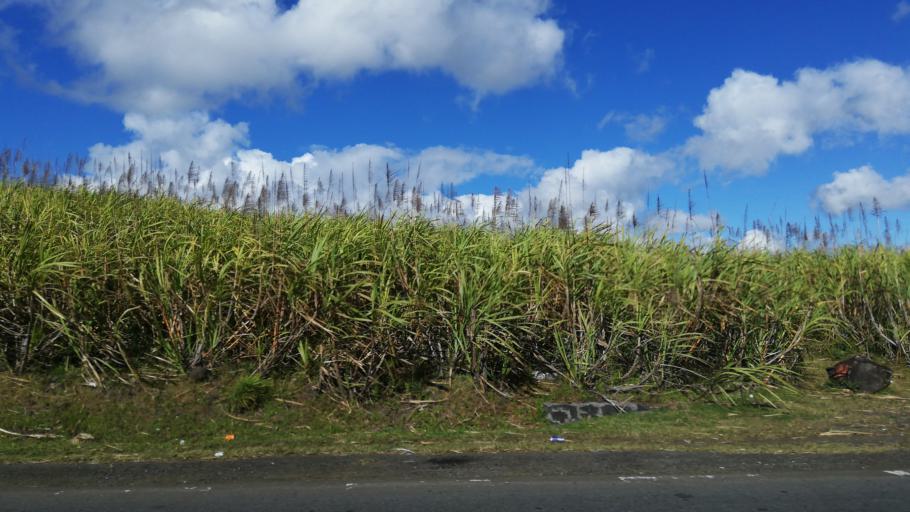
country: MU
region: Moka
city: Quartier Militaire
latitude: -20.2431
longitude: 57.5863
